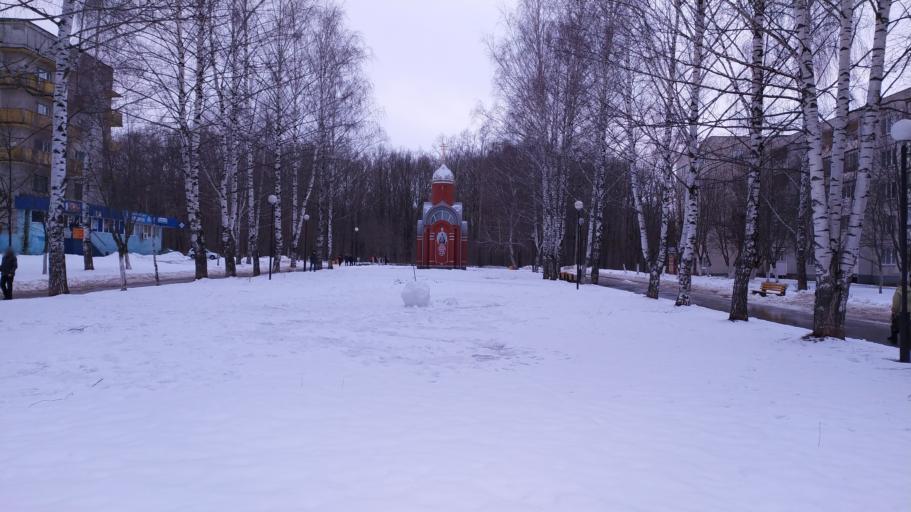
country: RU
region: Chuvashia
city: Novocheboksarsk
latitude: 56.1236
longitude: 47.4856
